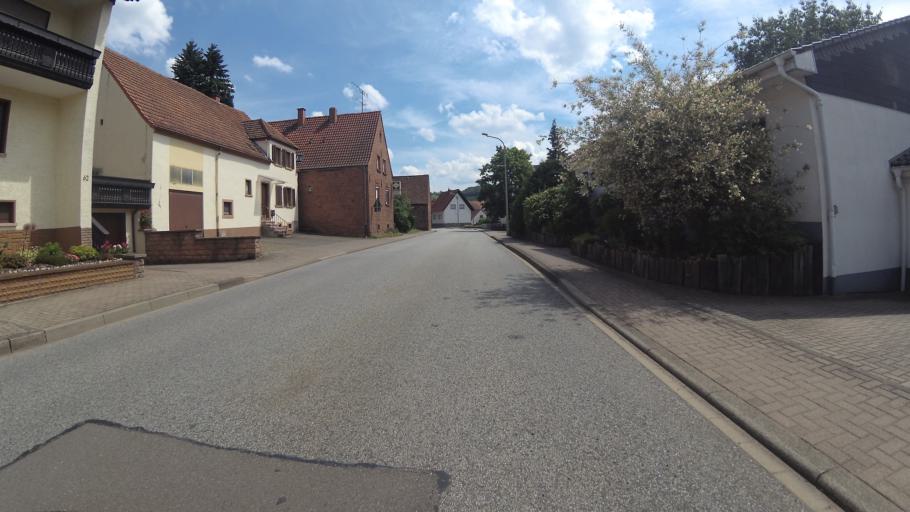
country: DE
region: Rheinland-Pfalz
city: Bann
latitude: 49.3928
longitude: 7.6112
